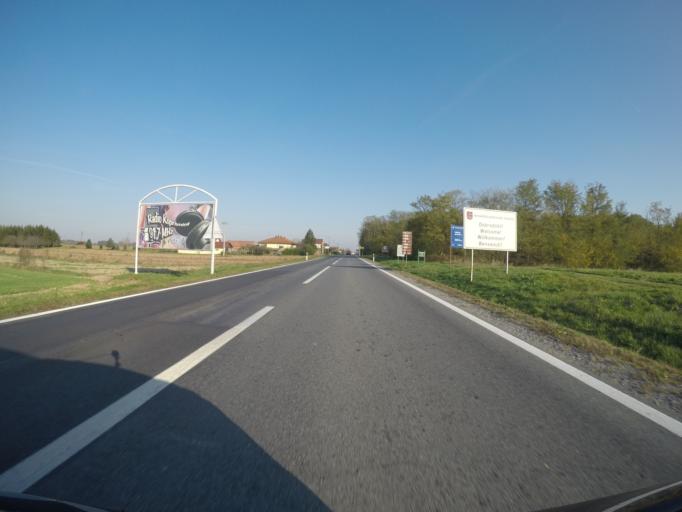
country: HR
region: Virovitick-Podravska
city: Pitomaca
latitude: 45.9690
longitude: 17.1875
